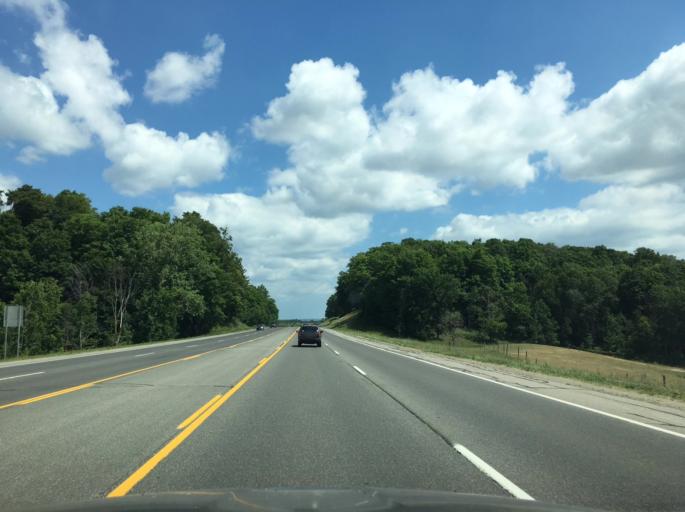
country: US
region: Michigan
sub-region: Grand Traverse County
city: Traverse City
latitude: 44.7104
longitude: -85.6506
